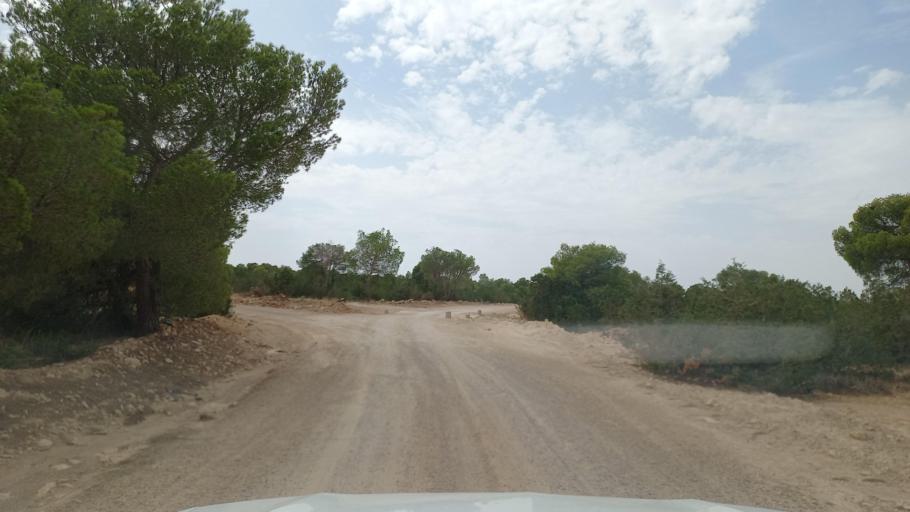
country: TN
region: Al Qasrayn
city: Kasserine
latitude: 35.3817
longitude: 8.8807
